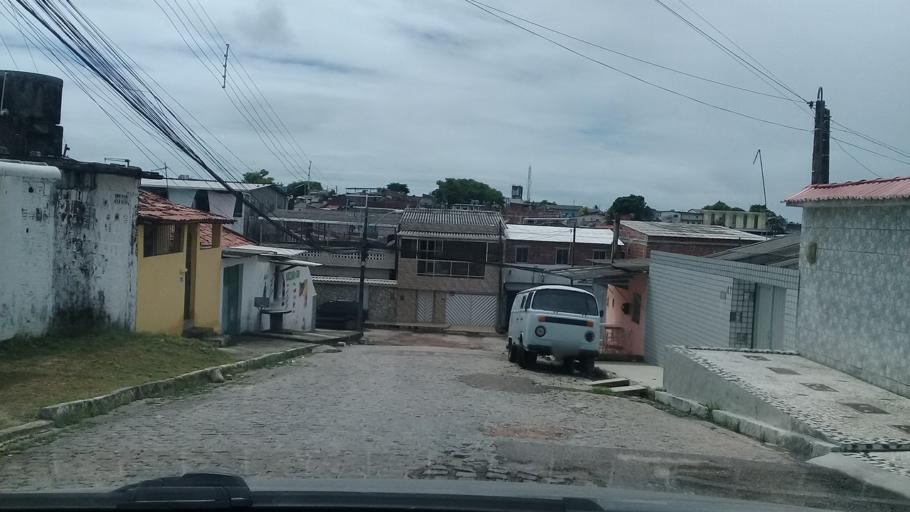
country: BR
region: Pernambuco
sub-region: Jaboatao Dos Guararapes
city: Jaboatao dos Guararapes
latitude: -8.1160
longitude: -34.9538
